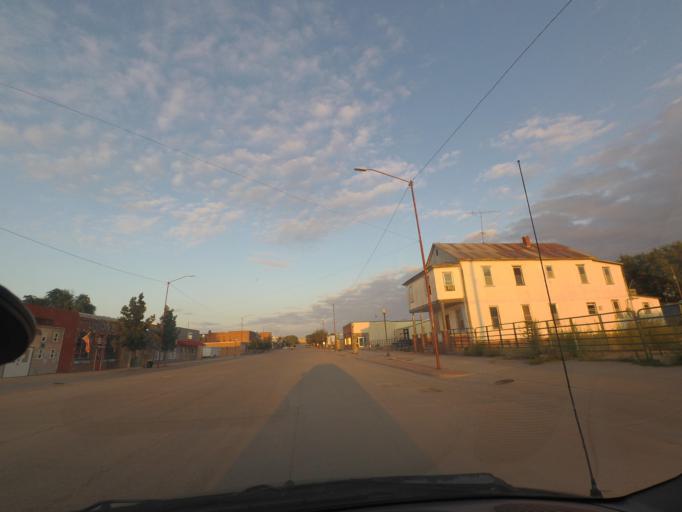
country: US
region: Kansas
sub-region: Cheyenne County
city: Saint Francis
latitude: 39.7742
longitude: -101.8051
